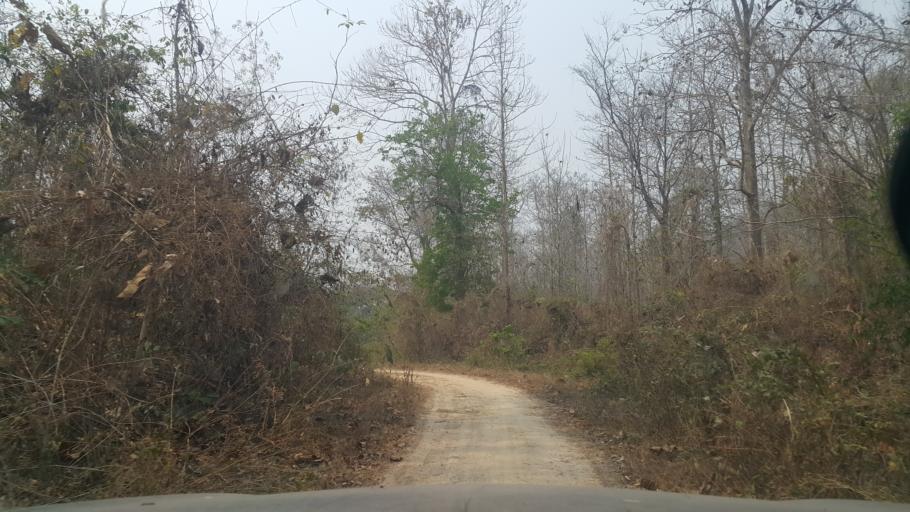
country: TH
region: Lampang
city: Hang Chat
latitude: 18.3187
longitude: 99.2468
